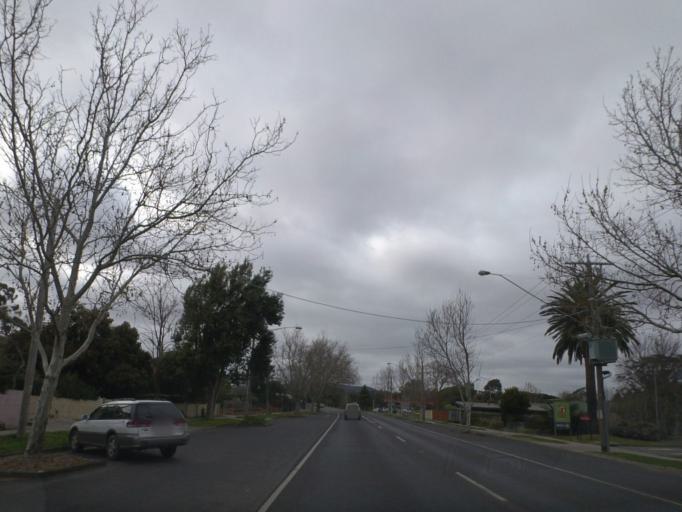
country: AU
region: Victoria
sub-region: Whittlesea
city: Whittlesea
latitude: -37.5110
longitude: 145.1195
